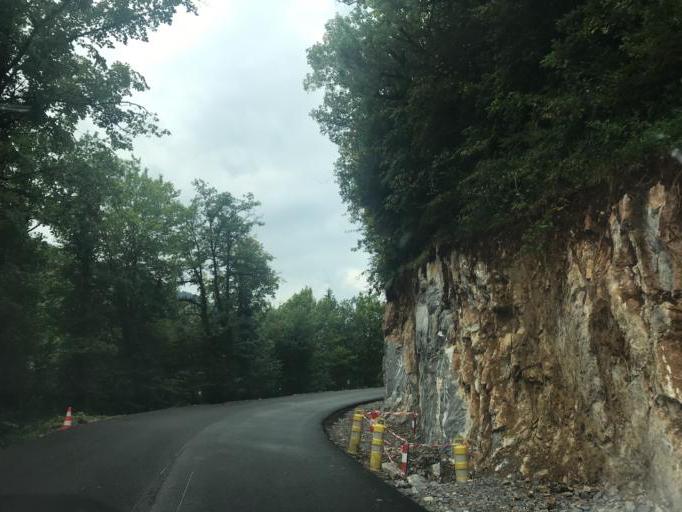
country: FR
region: Franche-Comte
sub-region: Departement du Jura
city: Saint-Claude
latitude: 46.3637
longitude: 5.8564
